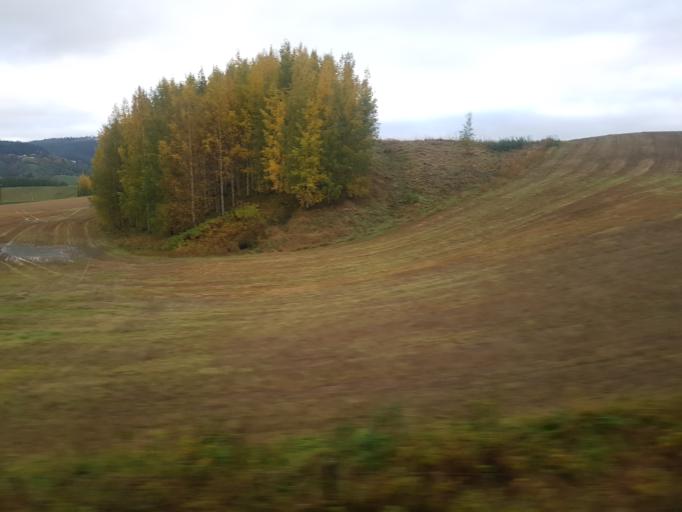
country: NO
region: Sor-Trondelag
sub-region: Melhus
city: Lundamo
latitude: 63.1929
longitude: 10.3072
